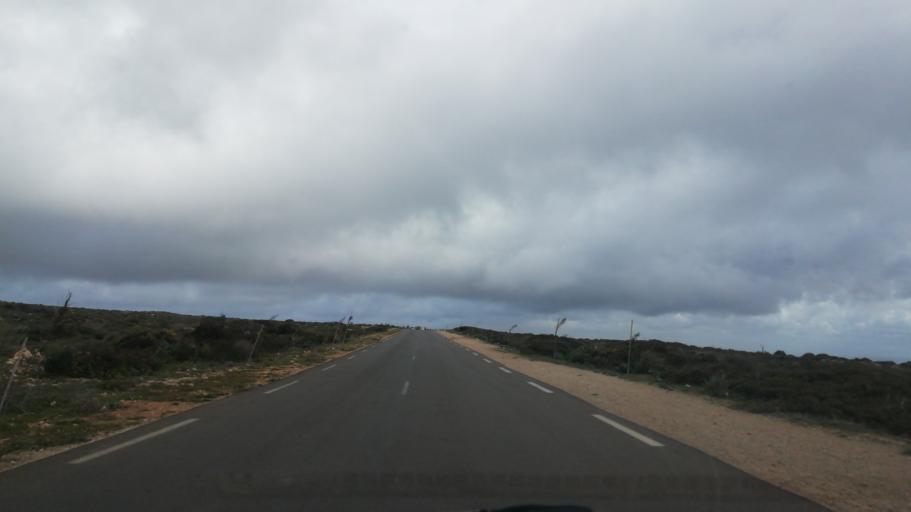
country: DZ
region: Oran
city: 'Ain el Turk
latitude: 35.6999
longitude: -0.7482
